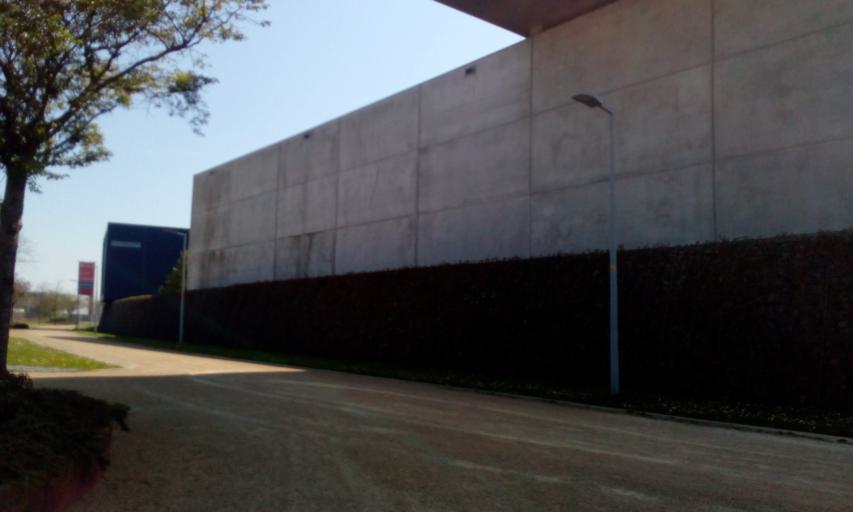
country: NL
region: South Holland
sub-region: Gemeente Kaag en Braassem
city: Oude Wetering
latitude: 52.2540
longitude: 4.6288
